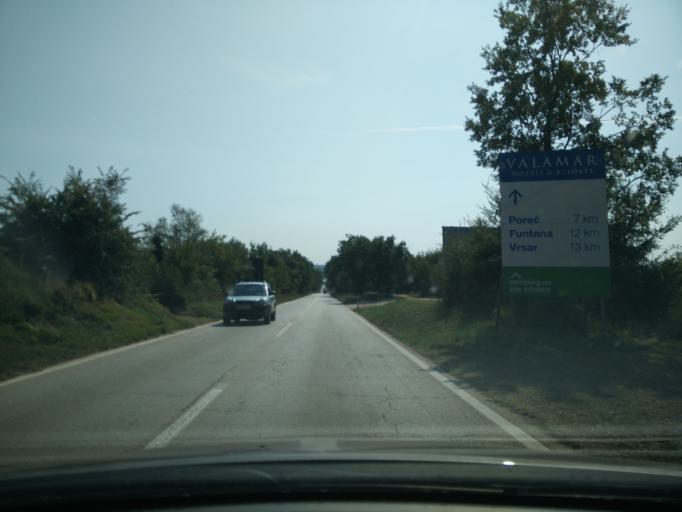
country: HR
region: Istarska
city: Novigrad
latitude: 45.2925
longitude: 13.6214
